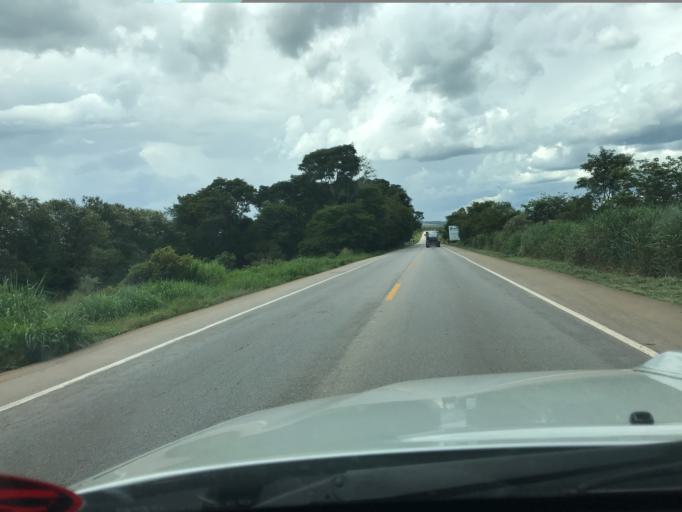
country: BR
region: Minas Gerais
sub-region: Ibia
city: Ibia
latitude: -19.5829
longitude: -46.4564
